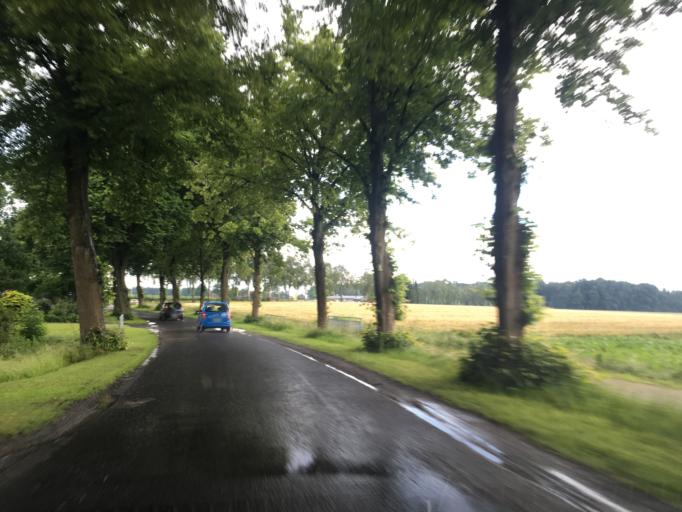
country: DE
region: North Rhine-Westphalia
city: Olfen
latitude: 51.7599
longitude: 7.3837
